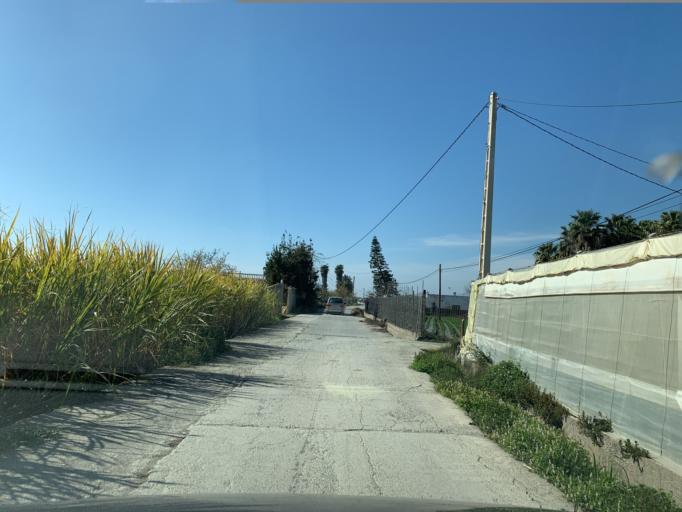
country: ES
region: Andalusia
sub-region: Provincia de Granada
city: El Varadero
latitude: 36.7260
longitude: -3.5504
